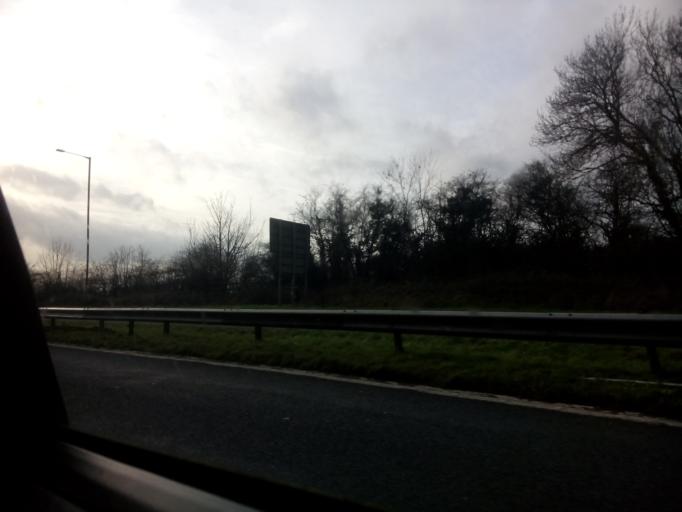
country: GB
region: England
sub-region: Worcestershire
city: Barnt Green
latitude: 52.3898
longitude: -2.0304
